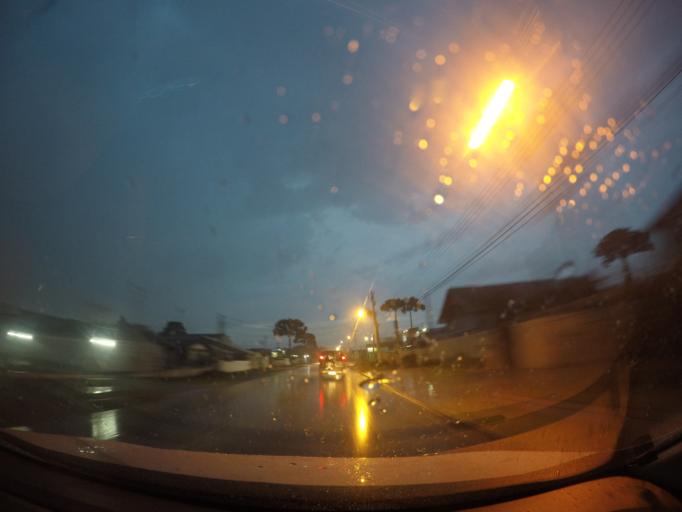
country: BR
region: Parana
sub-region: Sao Jose Dos Pinhais
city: Sao Jose dos Pinhais
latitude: -25.5006
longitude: -49.2340
